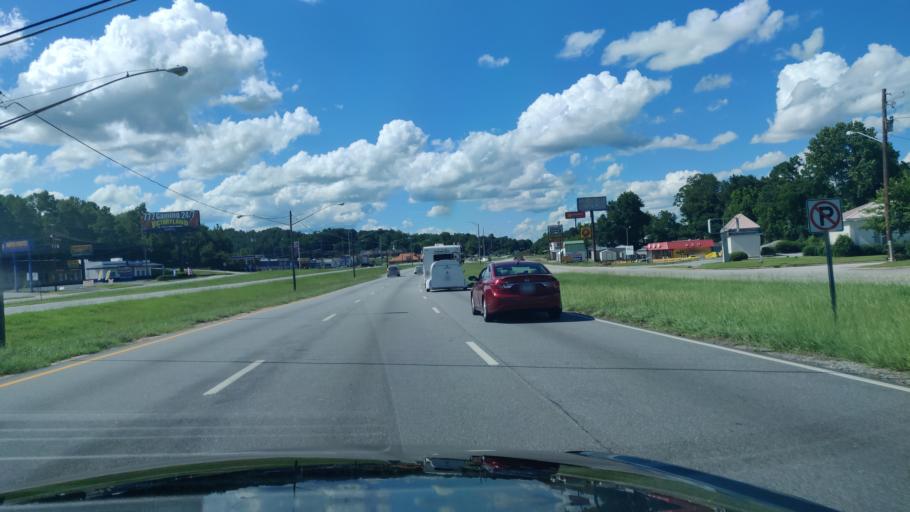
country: US
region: Alabama
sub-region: Russell County
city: Phenix City
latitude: 32.4694
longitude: -85.0287
